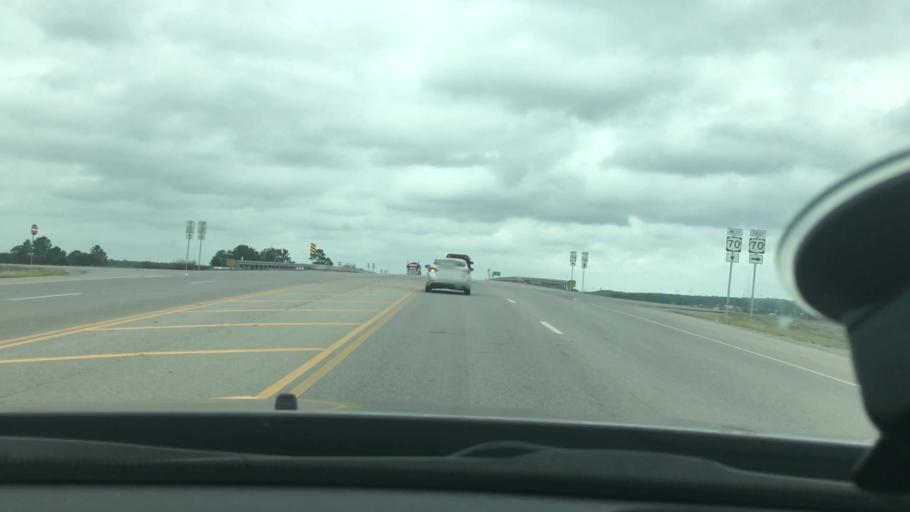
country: US
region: Oklahoma
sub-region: Bryan County
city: Durant
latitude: 33.9640
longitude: -96.3733
